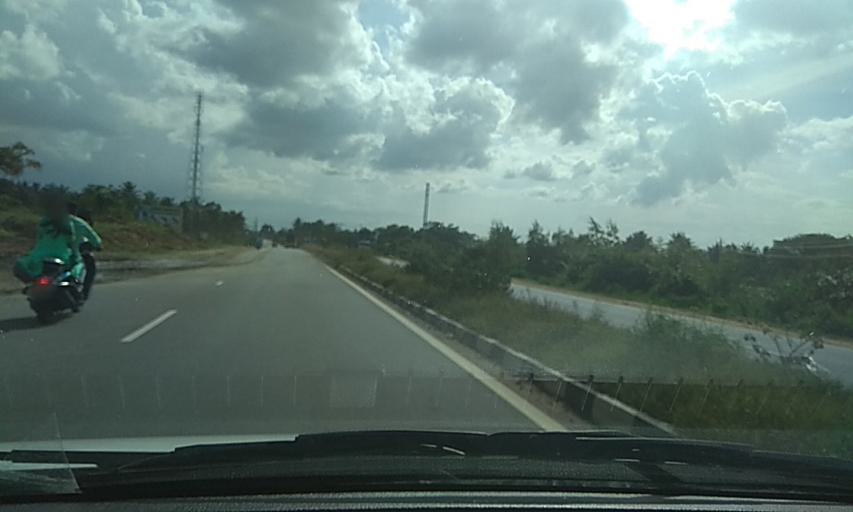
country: IN
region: Karnataka
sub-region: Mandya
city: Pandavapura
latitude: 12.4832
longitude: 76.7762
